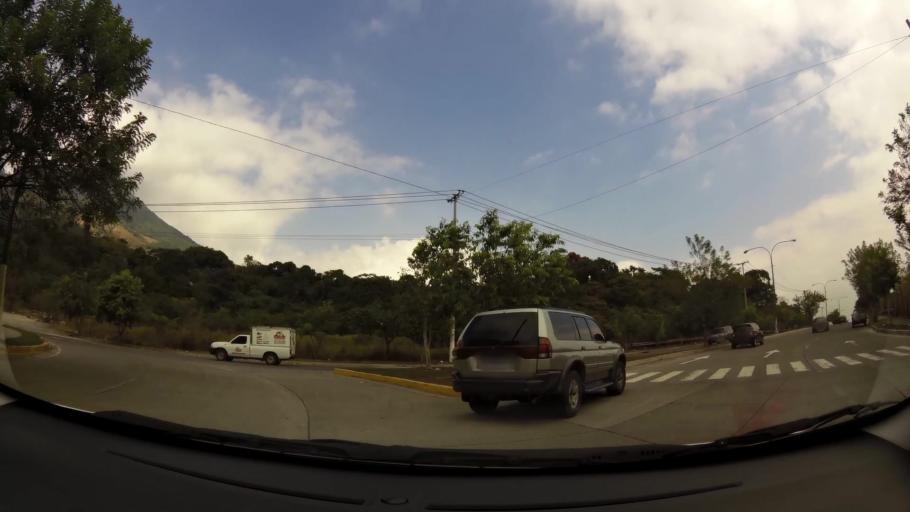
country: SV
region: San Salvador
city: Mejicanos
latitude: 13.7200
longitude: -89.2399
